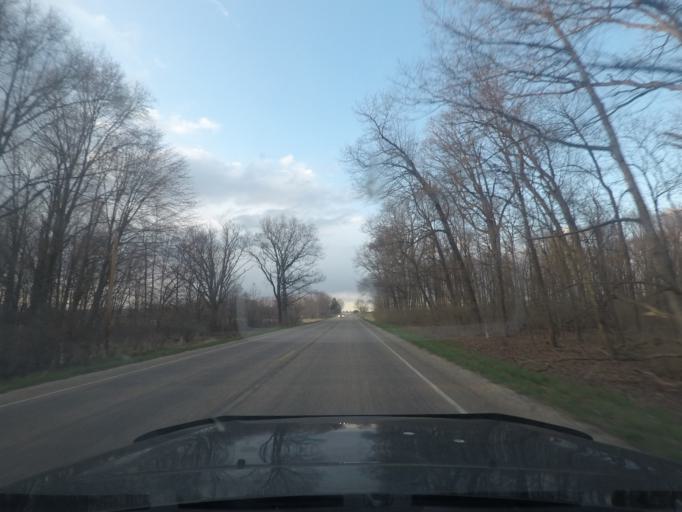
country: US
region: Indiana
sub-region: LaPorte County
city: LaPorte
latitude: 41.5583
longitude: -86.7396
